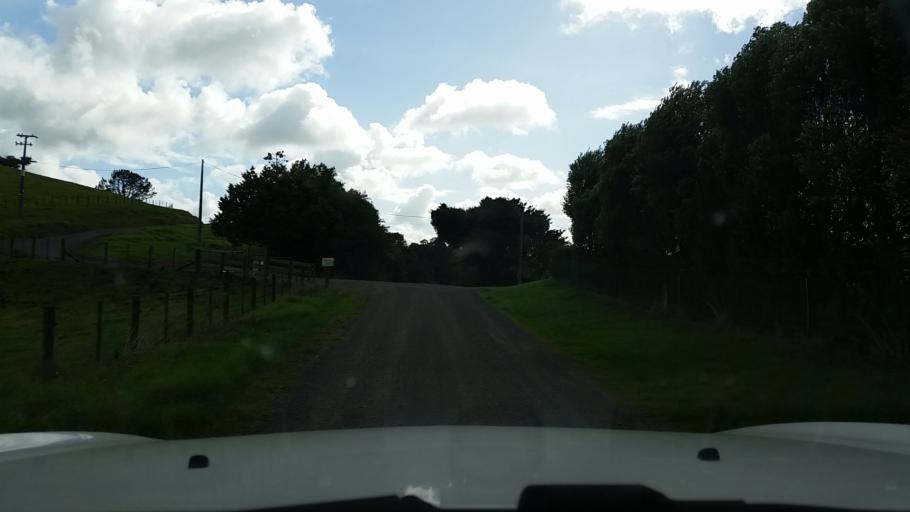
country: NZ
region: Waikato
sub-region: Hauraki District
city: Ngatea
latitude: -37.4583
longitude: 175.4692
